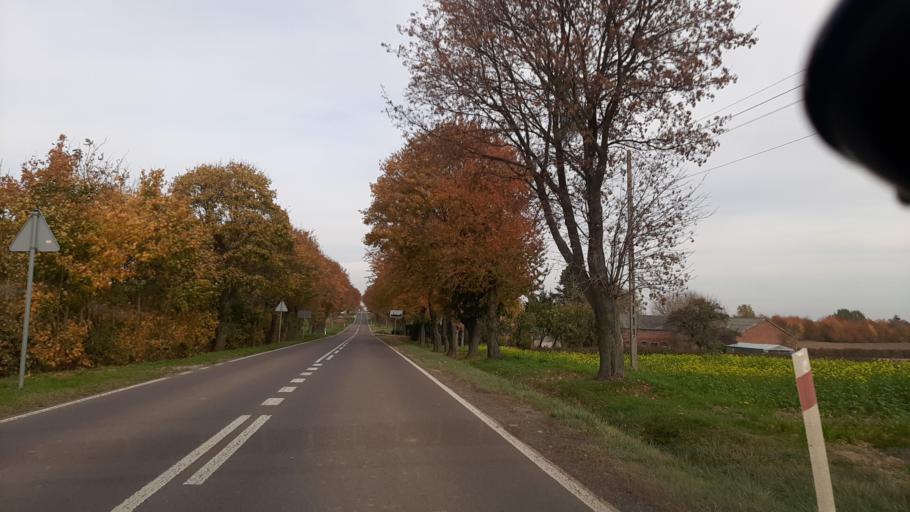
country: PL
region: Lublin Voivodeship
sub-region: Powiat pulawski
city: Markuszow
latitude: 51.3386
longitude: 22.2566
